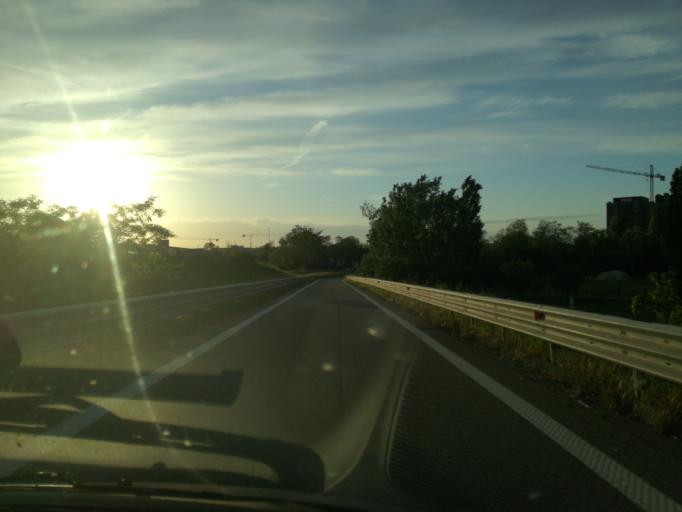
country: IT
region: Lombardy
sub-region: Citta metropolitana di Milano
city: Noverasco-Sporting Mirasole
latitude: 45.3908
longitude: 9.2133
